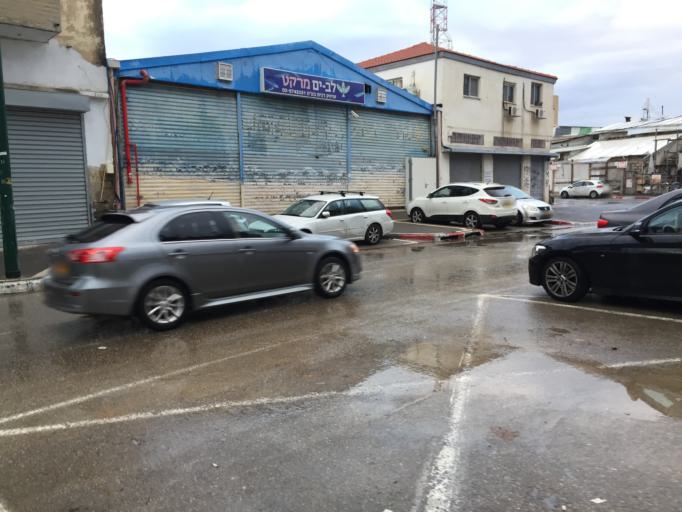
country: IL
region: Tel Aviv
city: Yafo
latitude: 32.0527
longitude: 34.7606
